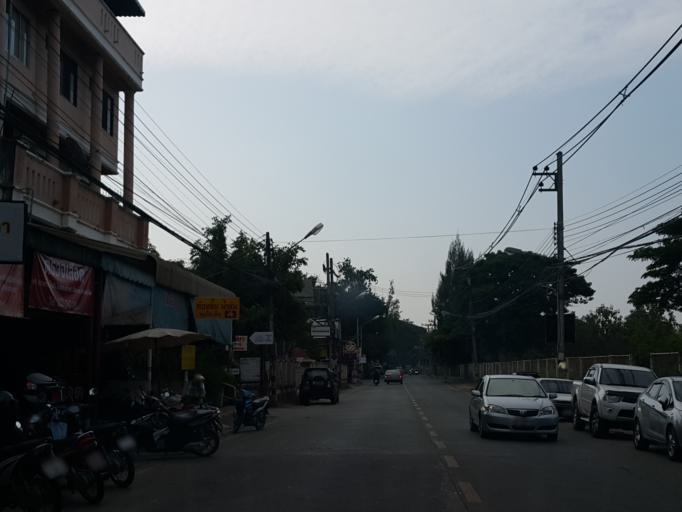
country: TH
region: Chiang Mai
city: Chiang Mai
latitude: 18.7885
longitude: 99.0179
